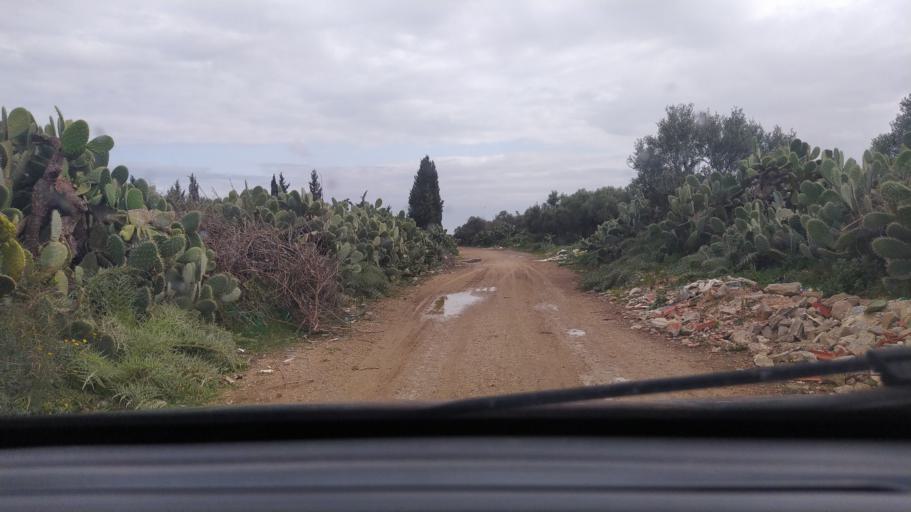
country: TN
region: Al Munastir
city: Sidi Bin Nur
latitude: 35.5168
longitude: 10.9296
